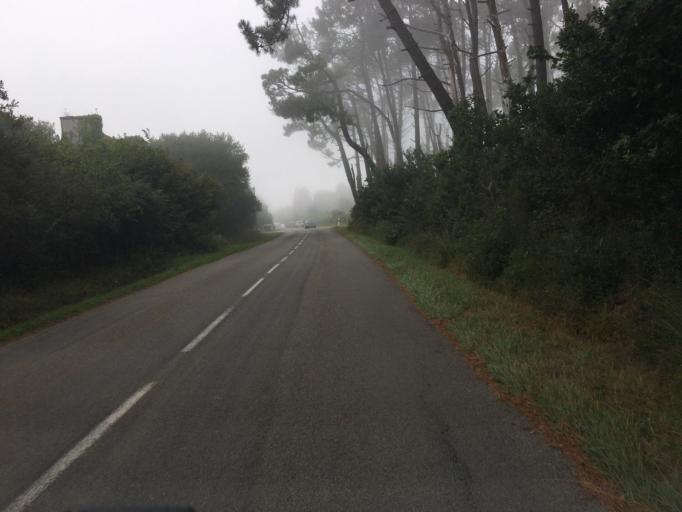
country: FR
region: Brittany
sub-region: Departement du Finistere
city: Plogoff
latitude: 48.0622
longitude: -4.6461
